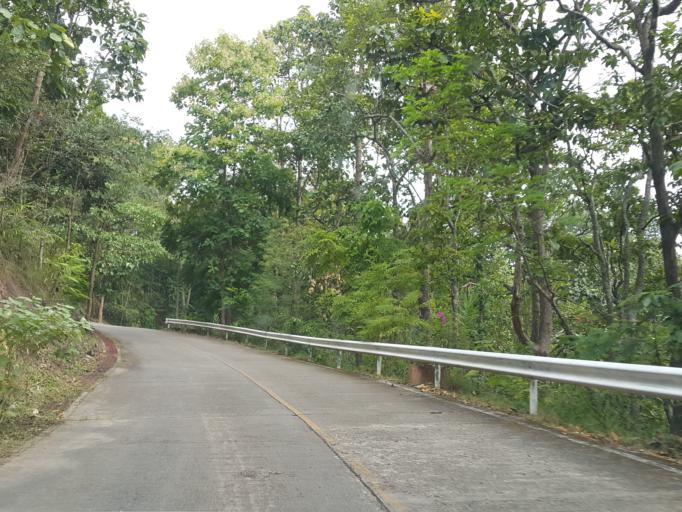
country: TH
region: Mae Hong Son
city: Mae Hong Son
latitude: 19.2986
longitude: 97.9599
